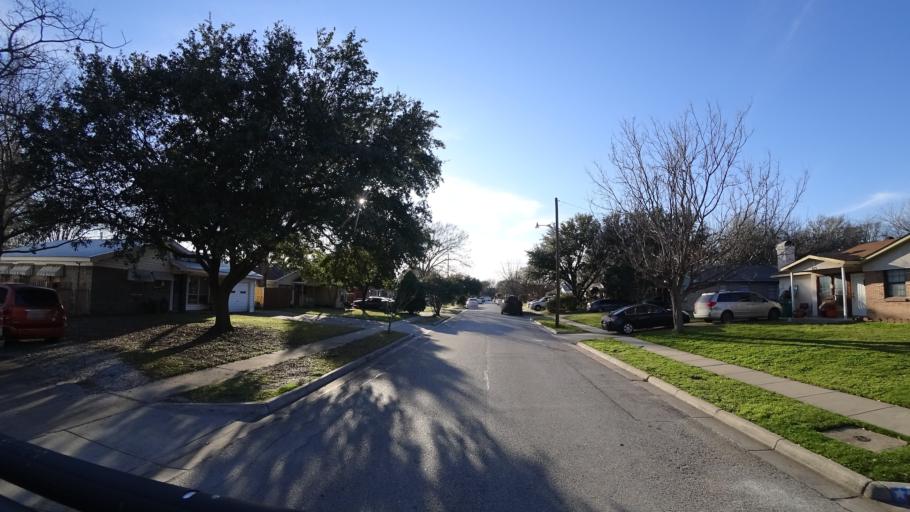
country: US
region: Texas
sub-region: Denton County
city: Lewisville
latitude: 33.0405
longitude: -97.0077
